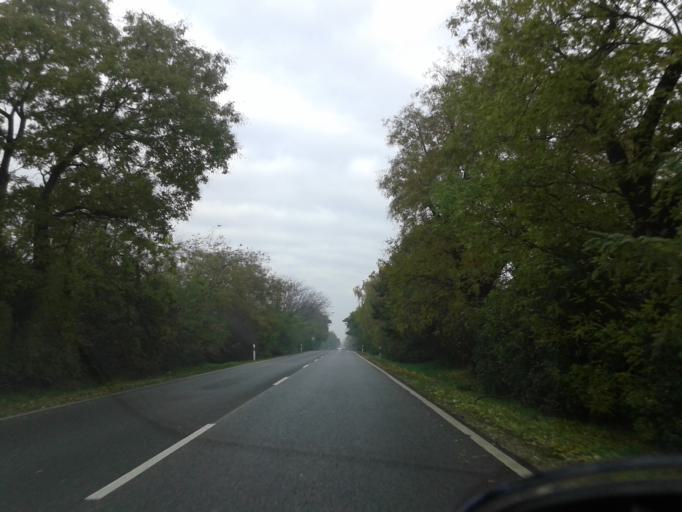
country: HU
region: Pest
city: Szazhalombatta
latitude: 47.3067
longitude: 18.8874
